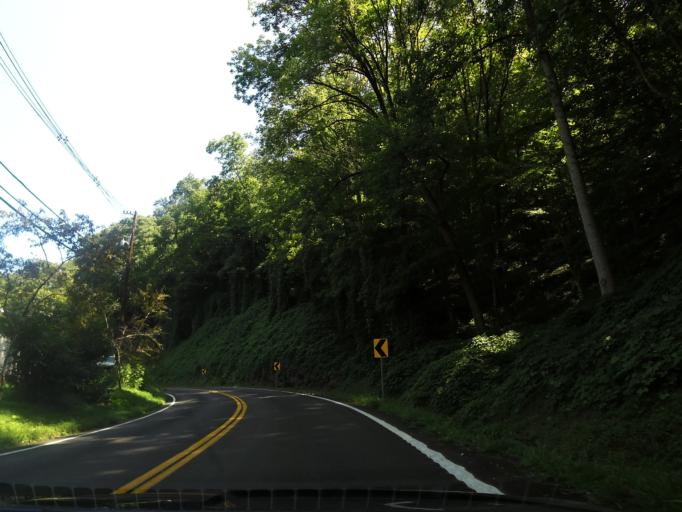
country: US
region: Kentucky
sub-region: Clay County
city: Manchester
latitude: 37.1028
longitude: -83.6659
